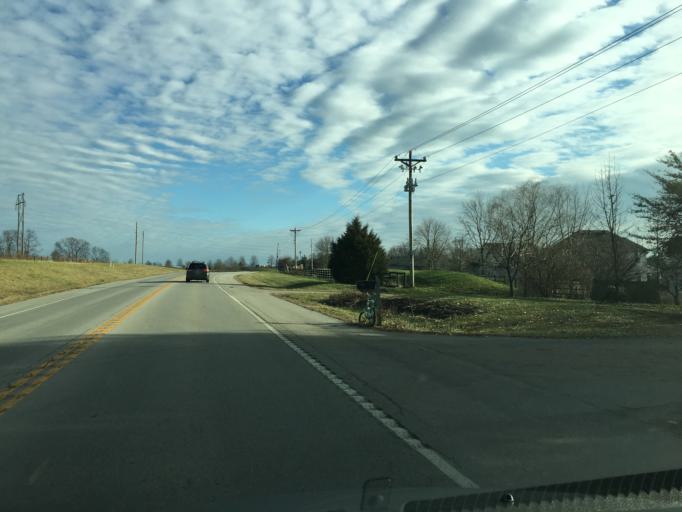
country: US
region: Kentucky
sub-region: Scott County
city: Georgetown
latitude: 38.2416
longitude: -84.5798
